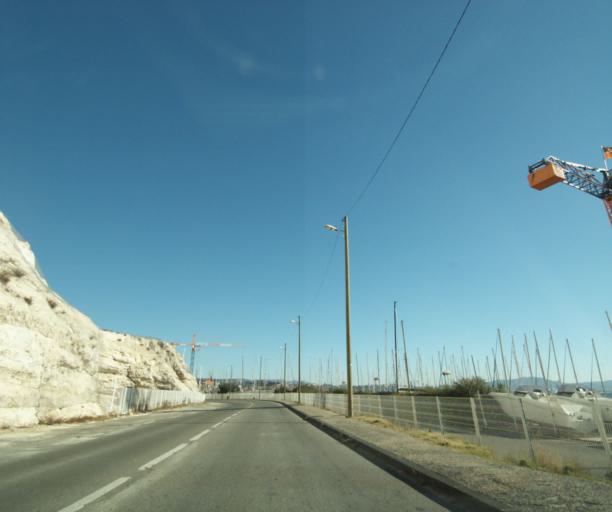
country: FR
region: Provence-Alpes-Cote d'Azur
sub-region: Departement des Bouches-du-Rhone
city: Marseille 16
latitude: 43.3604
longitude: 5.2973
